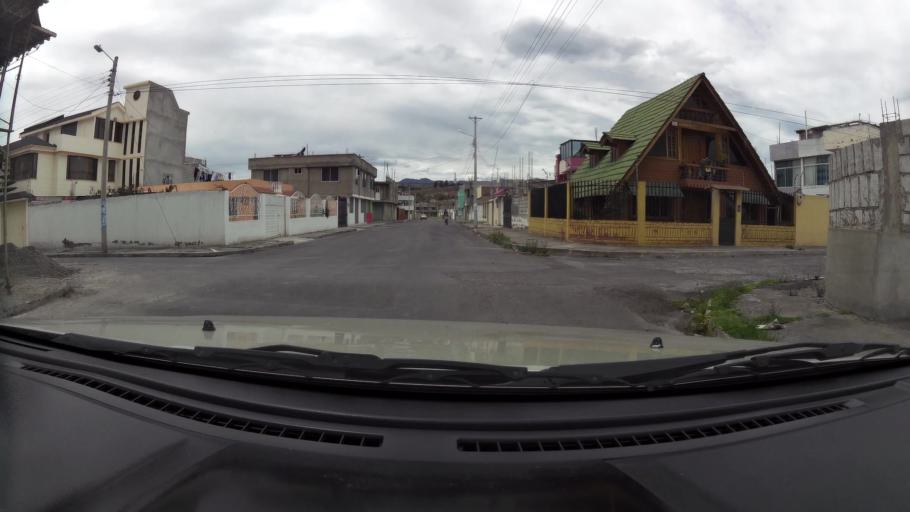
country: EC
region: Cotopaxi
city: Latacunga
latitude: -0.9526
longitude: -78.6028
